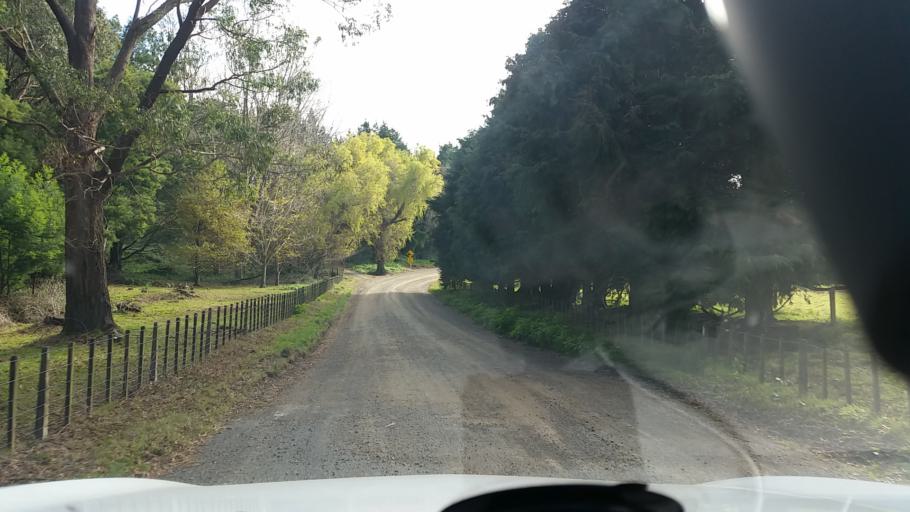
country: NZ
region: Hawke's Bay
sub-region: Napier City
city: Napier
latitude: -39.1339
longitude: 176.8961
